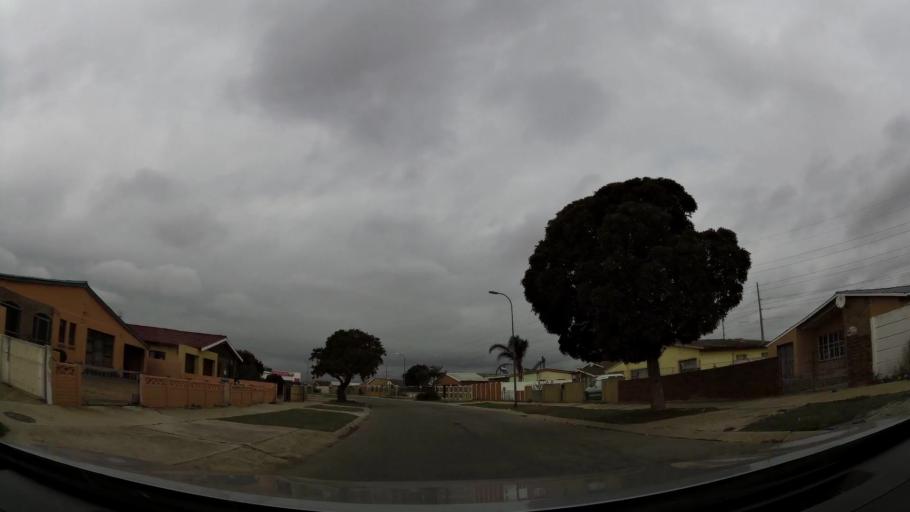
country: ZA
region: Eastern Cape
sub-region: Nelson Mandela Bay Metropolitan Municipality
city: Port Elizabeth
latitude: -33.9004
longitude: 25.5524
